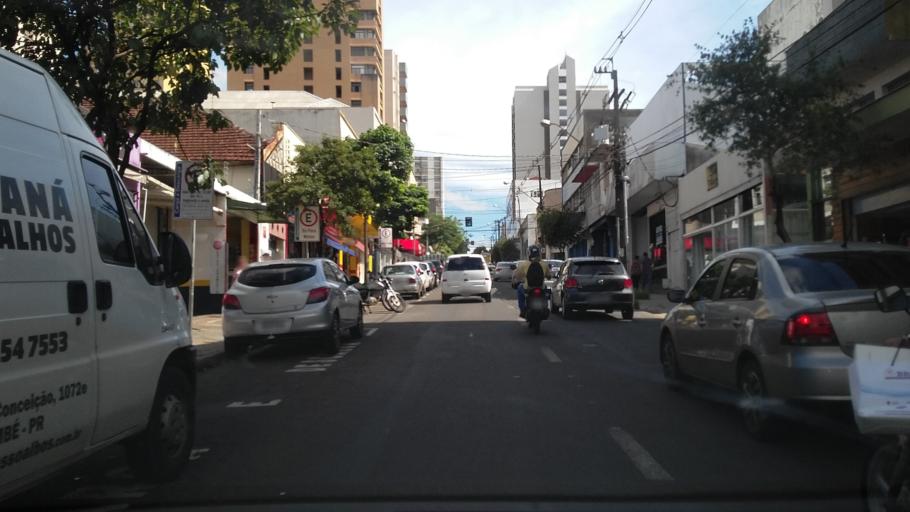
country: BR
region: Parana
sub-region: Londrina
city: Londrina
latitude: -23.3091
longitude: -51.1628
